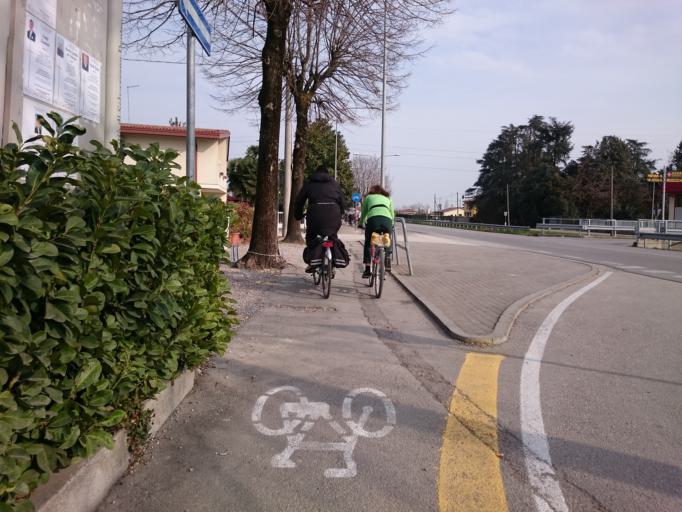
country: IT
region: Veneto
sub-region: Provincia di Padova
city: Caselle
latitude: 45.4091
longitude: 11.8235
